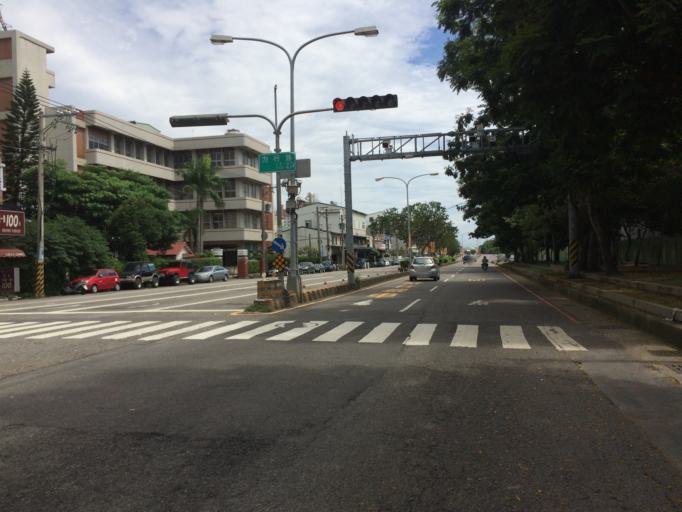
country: TW
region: Taiwan
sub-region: Taichung City
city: Taichung
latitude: 24.1506
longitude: 120.6982
